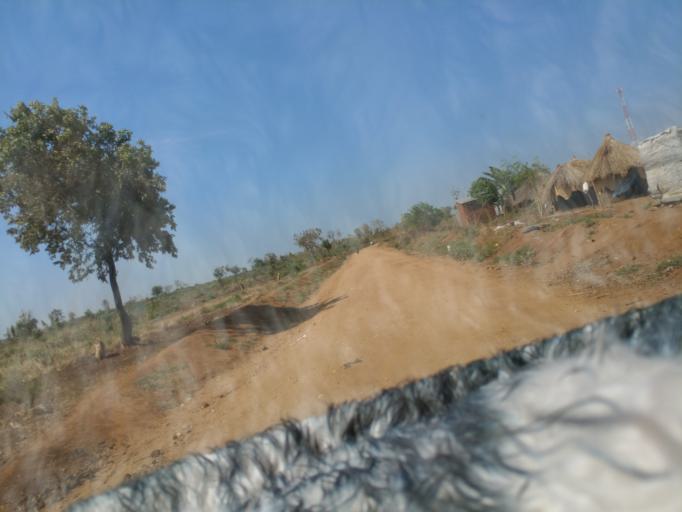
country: UG
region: Northern Region
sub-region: Yumbe District
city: Yumbe
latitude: 3.3912
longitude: 31.3381
